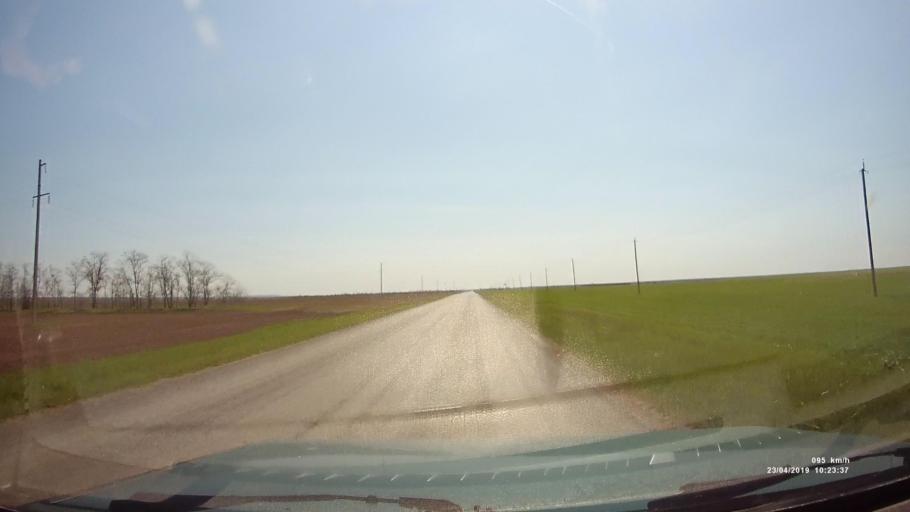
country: RU
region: Rostov
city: Sovetskoye
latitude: 46.6459
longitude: 42.4276
